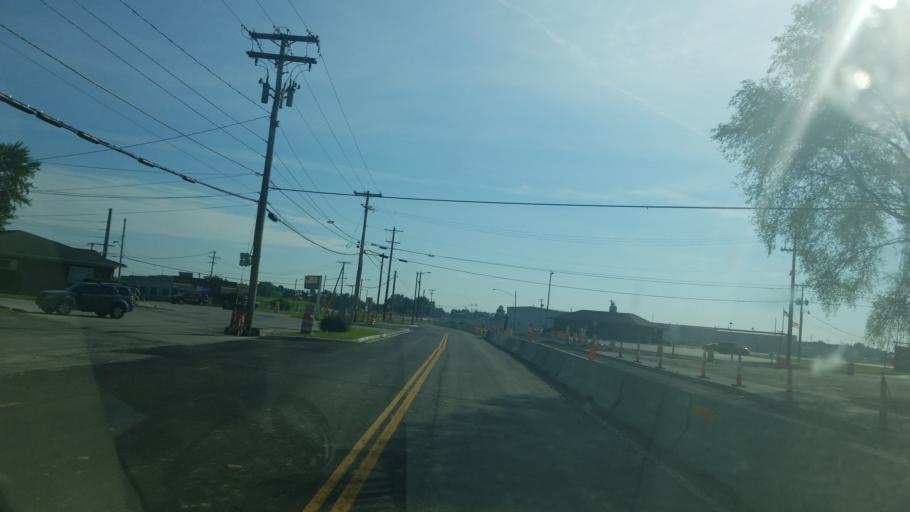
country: US
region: Ohio
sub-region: Hancock County
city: Findlay
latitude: 41.0211
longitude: -83.6704
